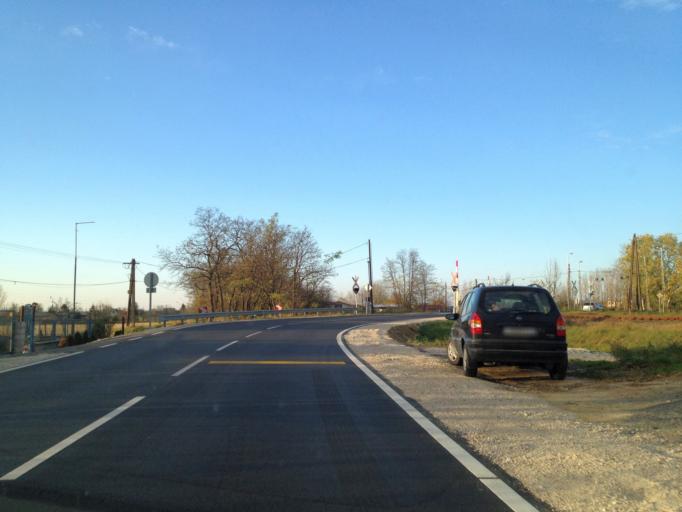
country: HU
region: Gyor-Moson-Sopron
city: Gyorujbarat
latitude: 47.6420
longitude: 17.6631
